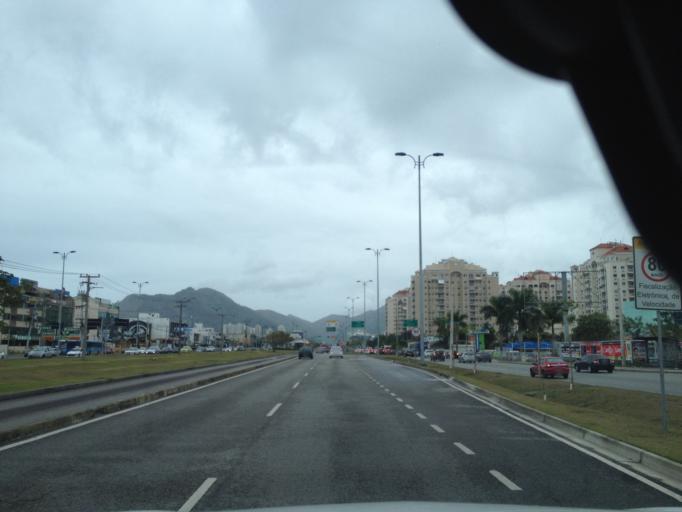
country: BR
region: Rio de Janeiro
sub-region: Nilopolis
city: Nilopolis
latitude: -23.0145
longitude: -43.4679
